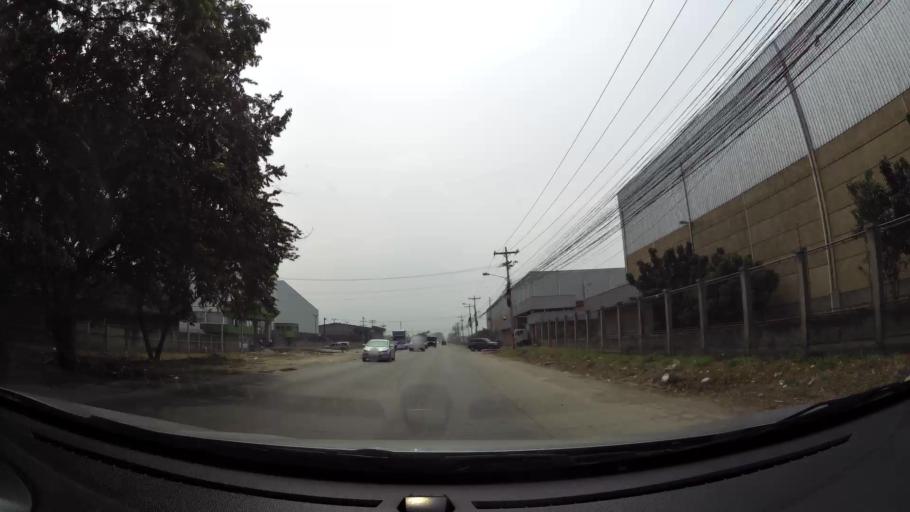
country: HN
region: Cortes
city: Chotepe
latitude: 15.4666
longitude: -87.9789
